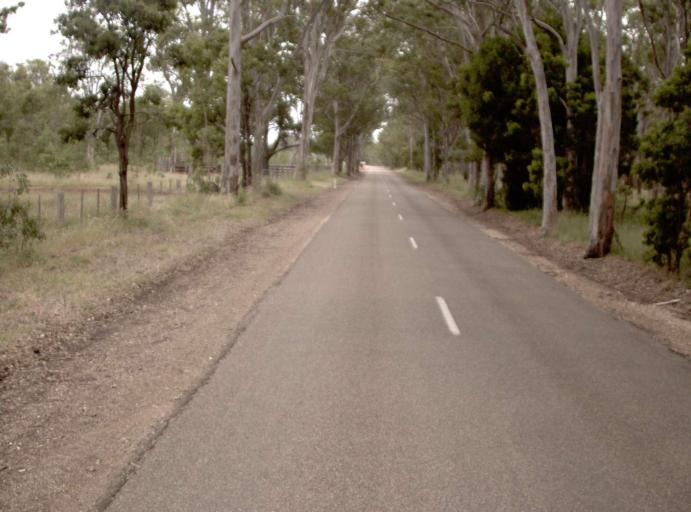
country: AU
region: Victoria
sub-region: Wellington
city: Sale
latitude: -37.8611
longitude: 147.0691
